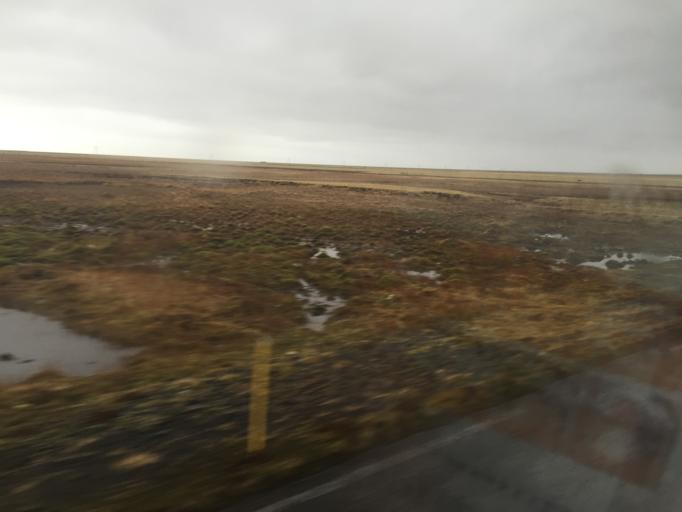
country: IS
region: East
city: Hoefn
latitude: 63.8969
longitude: -16.7017
